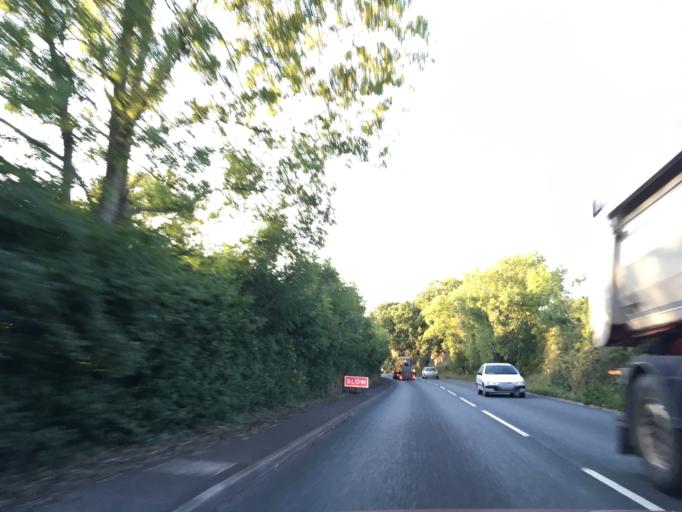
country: GB
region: England
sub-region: Bath and North East Somerset
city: Publow
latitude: 51.3621
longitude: -2.5426
